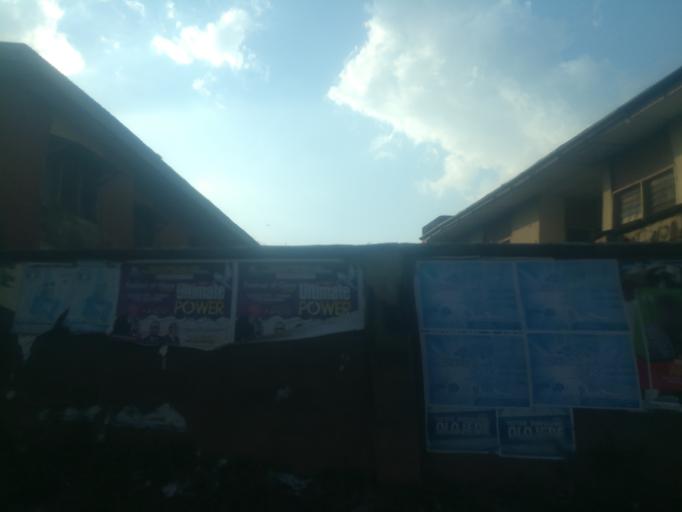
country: NG
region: Oyo
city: Moniya
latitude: 7.4571
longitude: 3.9176
